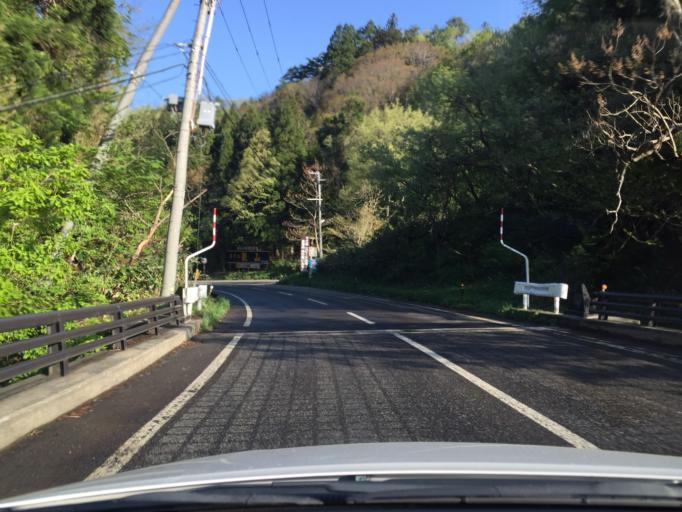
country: JP
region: Fukushima
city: Kitakata
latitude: 37.6686
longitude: 139.9954
